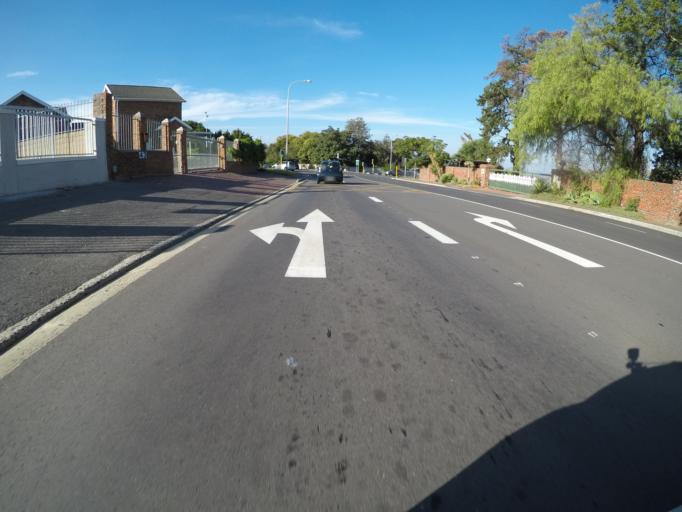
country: ZA
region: Western Cape
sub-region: City of Cape Town
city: Kraaifontein
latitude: -33.8724
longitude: 18.6489
